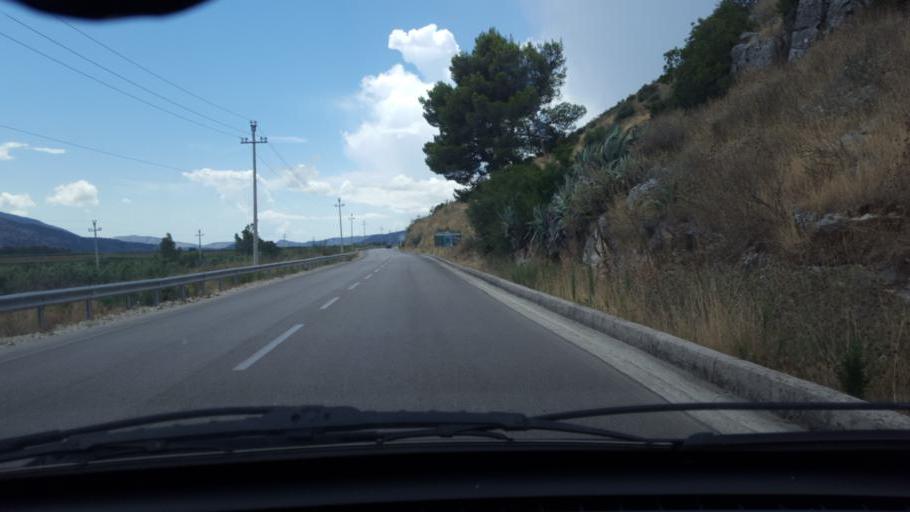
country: AL
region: Vlore
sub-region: Rrethi i Sarandes
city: Sarande
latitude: 39.8320
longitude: 20.0226
